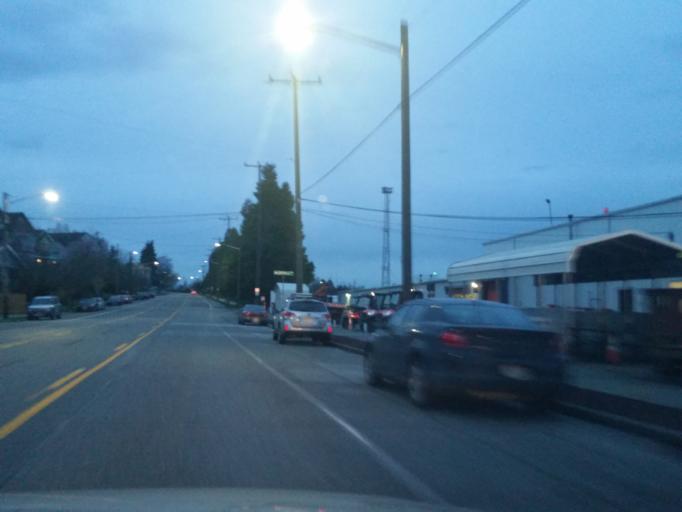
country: US
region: Washington
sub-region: King County
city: Seattle
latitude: 47.6519
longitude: -122.3829
